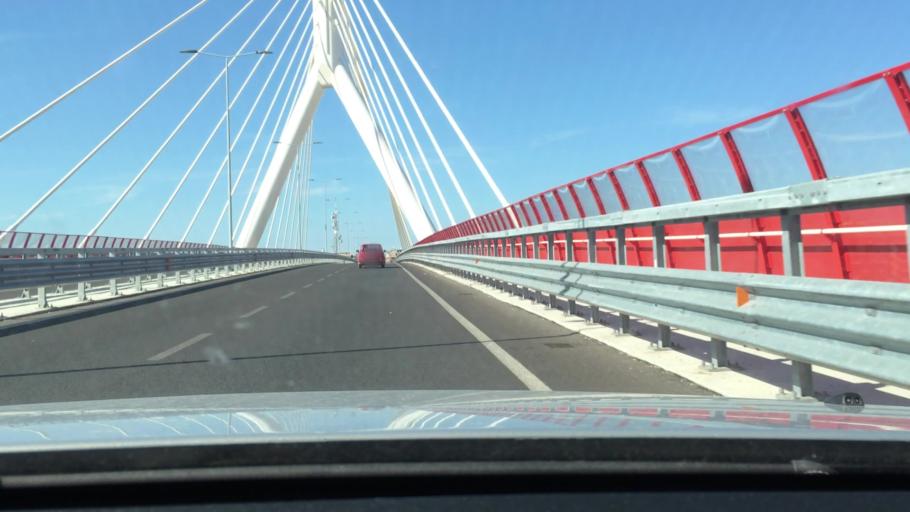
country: IT
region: Apulia
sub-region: Provincia di Bari
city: Bari
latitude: 41.1181
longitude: 16.8485
